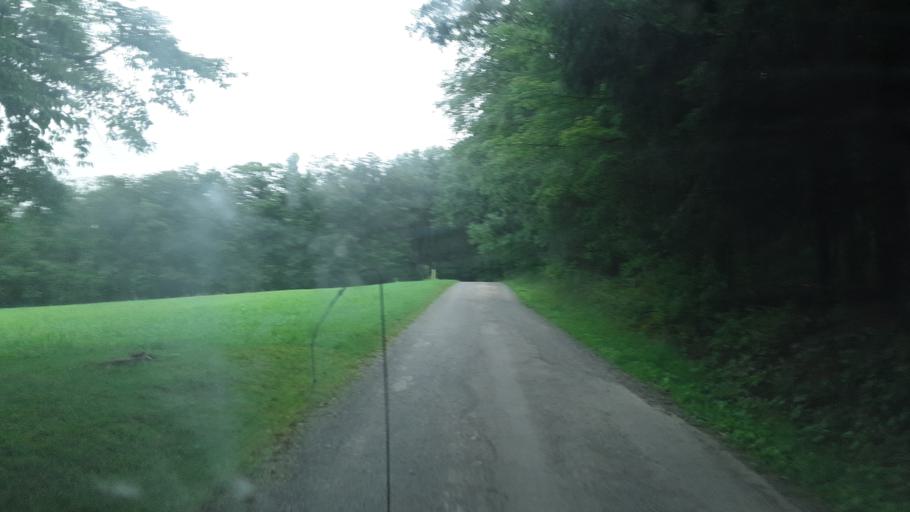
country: US
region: Pennsylvania
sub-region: Jefferson County
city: Punxsutawney
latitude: 40.9673
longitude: -79.1279
